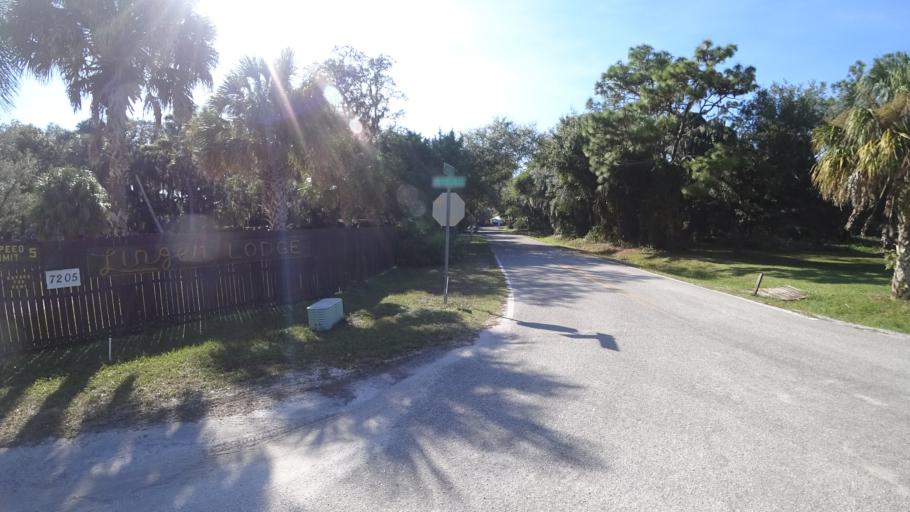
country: US
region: Florida
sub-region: Sarasota County
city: The Meadows
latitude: 27.4131
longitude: -82.4488
